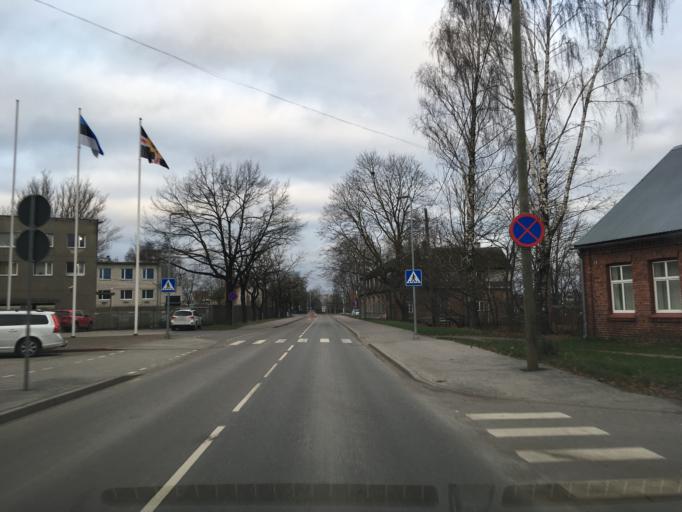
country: EE
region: Paernumaa
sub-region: Paernu linn
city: Parnu
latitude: 58.3871
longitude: 24.5094
